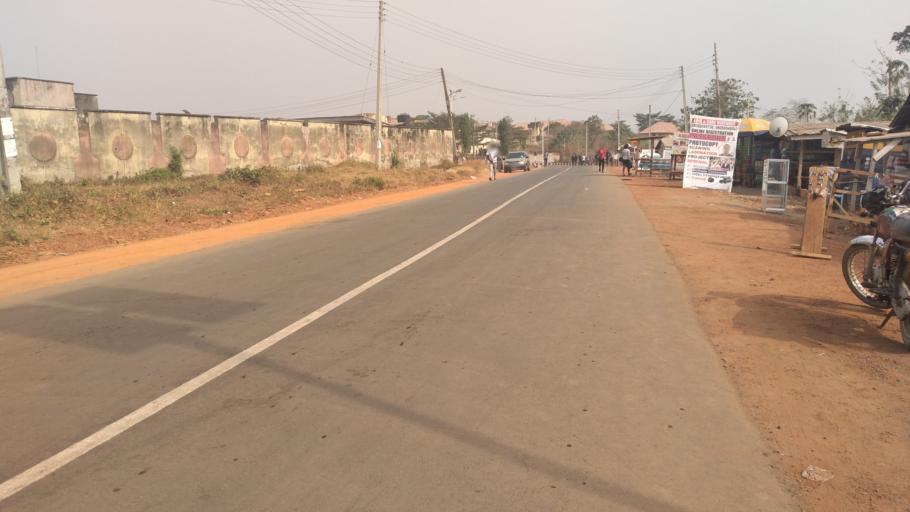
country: NG
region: Ondo
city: Ilare
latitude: 7.3026
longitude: 5.1415
